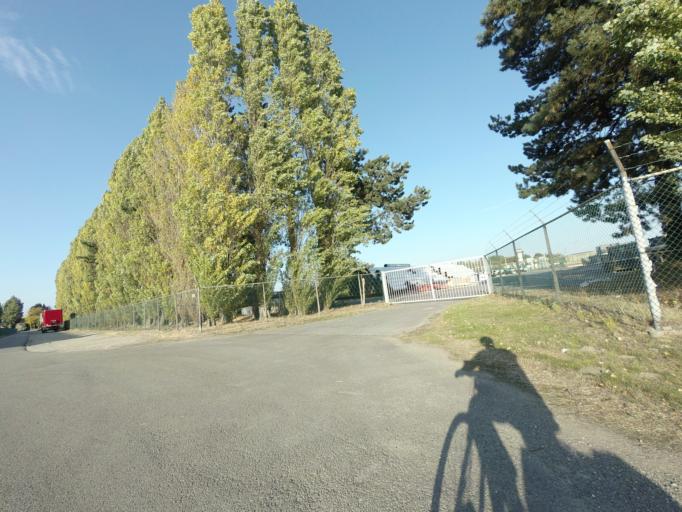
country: BE
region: Flanders
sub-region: Provincie Vlaams-Brabant
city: Haacht
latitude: 50.9408
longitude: 4.6264
